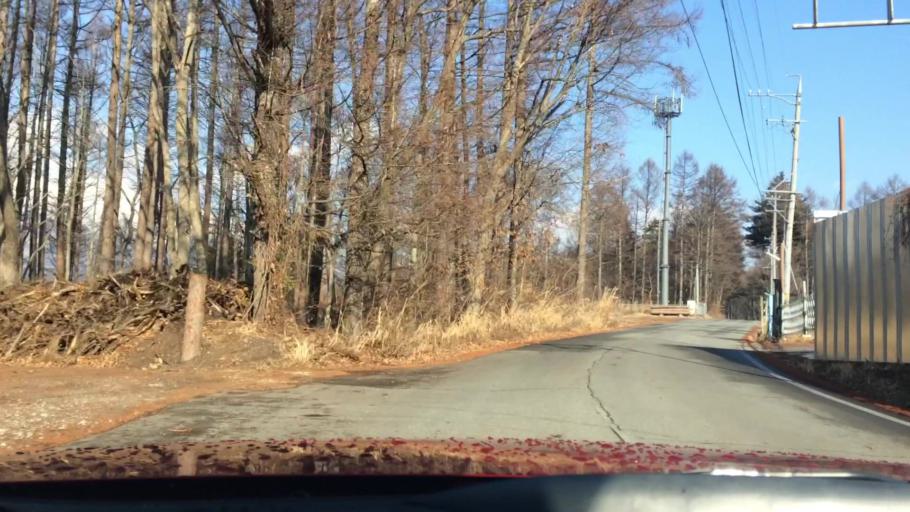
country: JP
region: Nagano
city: Komoro
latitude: 36.3179
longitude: 138.5498
